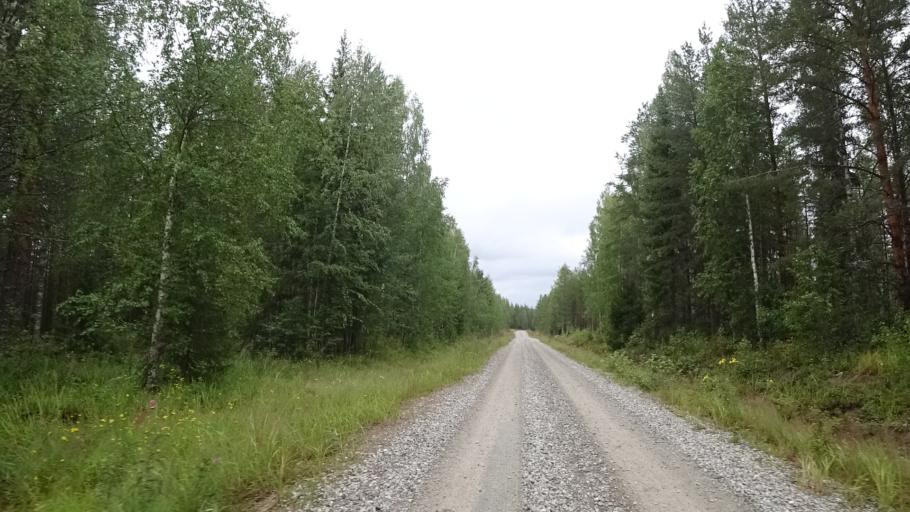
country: FI
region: North Karelia
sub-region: Pielisen Karjala
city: Lieksa
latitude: 63.4757
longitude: 30.2623
